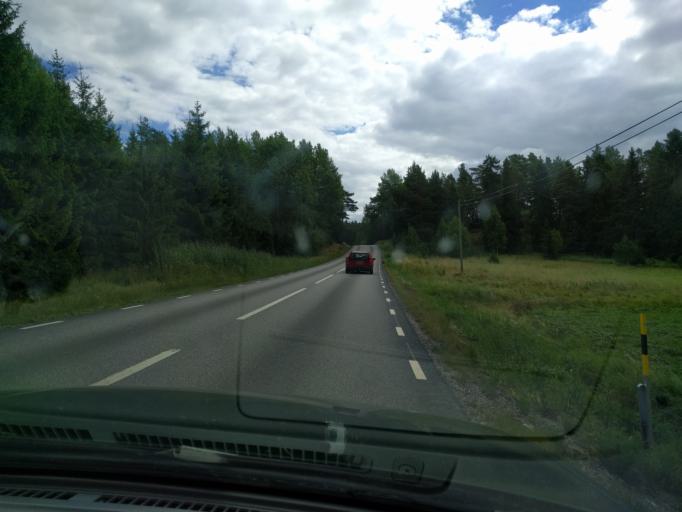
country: SE
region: Soedermanland
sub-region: Nykopings Kommun
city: Svalsta
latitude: 58.5199
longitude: 16.7839
